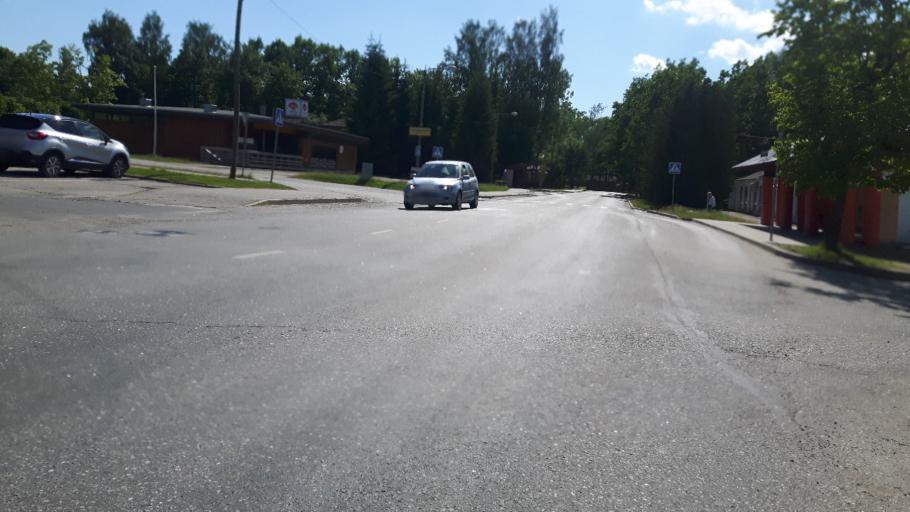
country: EE
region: Paernumaa
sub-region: Sindi linn
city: Sindi
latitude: 58.4082
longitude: 24.6593
